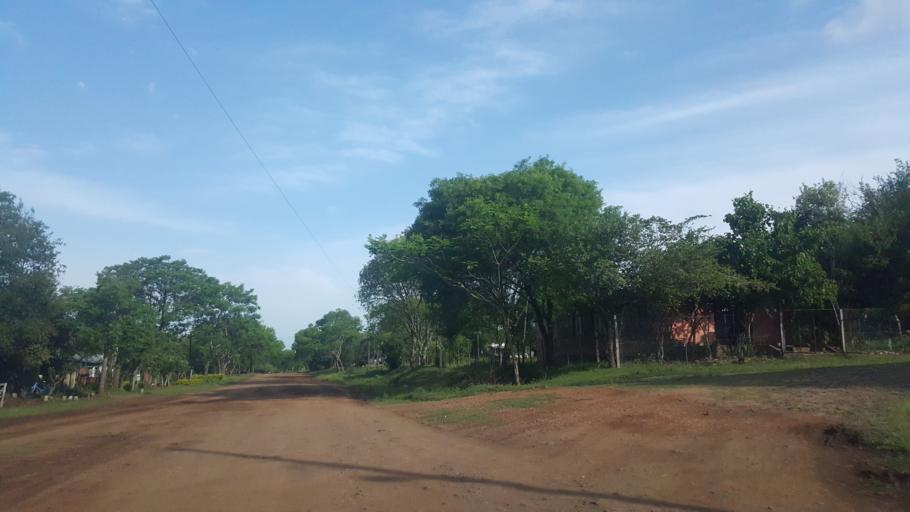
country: AR
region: Misiones
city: Cerro Cora
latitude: -27.5602
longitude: -55.7040
